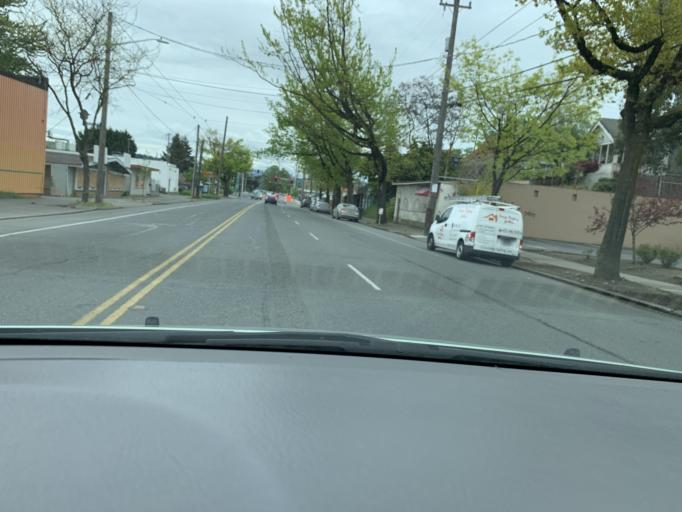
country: US
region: Washington
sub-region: King County
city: Bryn Mawr-Skyway
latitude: 47.5199
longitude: -122.2647
